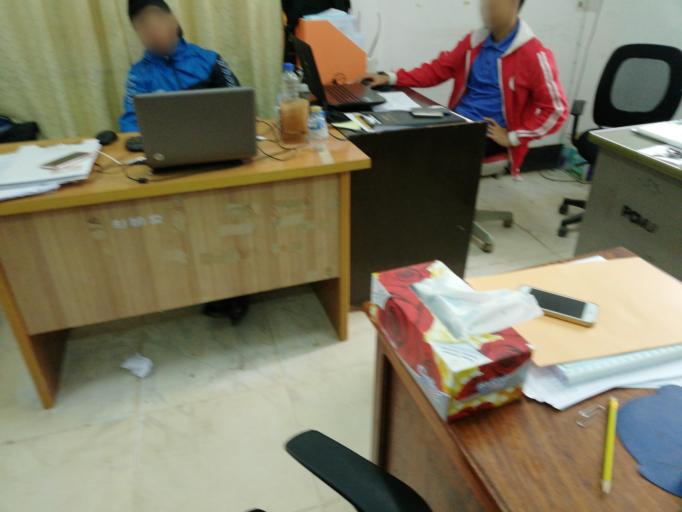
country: LA
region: Loungnamtha
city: Louang Namtha
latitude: 21.0085
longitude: 101.4058
